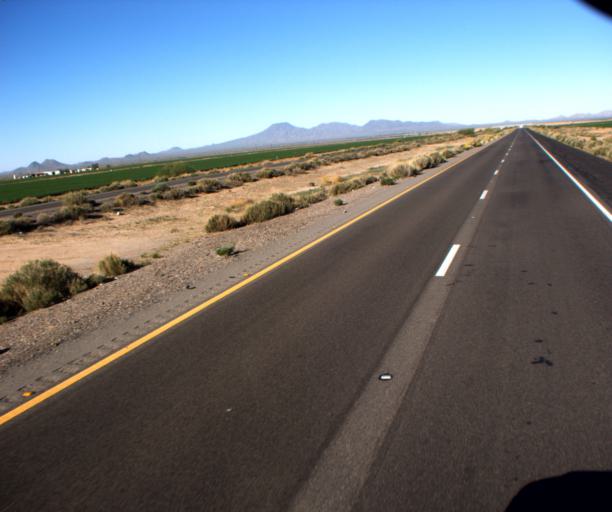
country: US
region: Arizona
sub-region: Pinal County
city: Casa Grande
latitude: 32.8283
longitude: -111.8965
